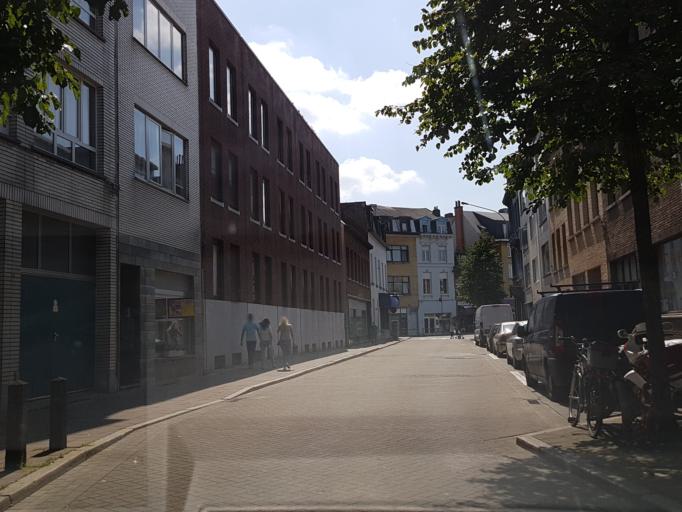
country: BE
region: Flanders
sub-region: Provincie Antwerpen
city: Antwerpen
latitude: 51.2253
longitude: 4.4197
